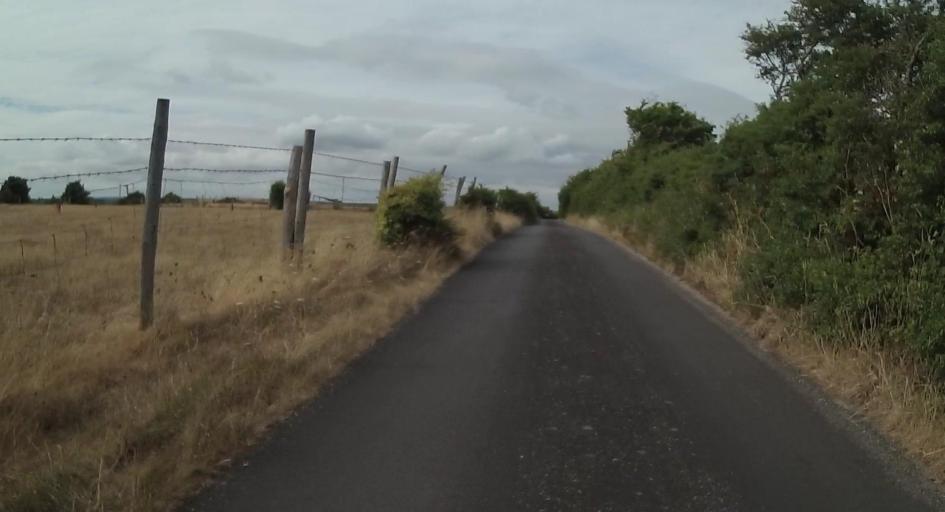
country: GB
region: England
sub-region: Dorset
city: Wareham
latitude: 50.6625
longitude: -2.0859
